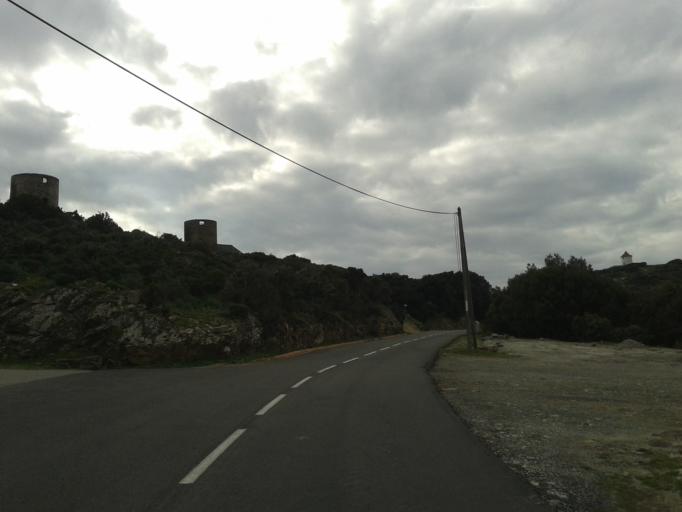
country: FR
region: Corsica
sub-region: Departement de la Haute-Corse
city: Brando
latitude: 42.9731
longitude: 9.3697
